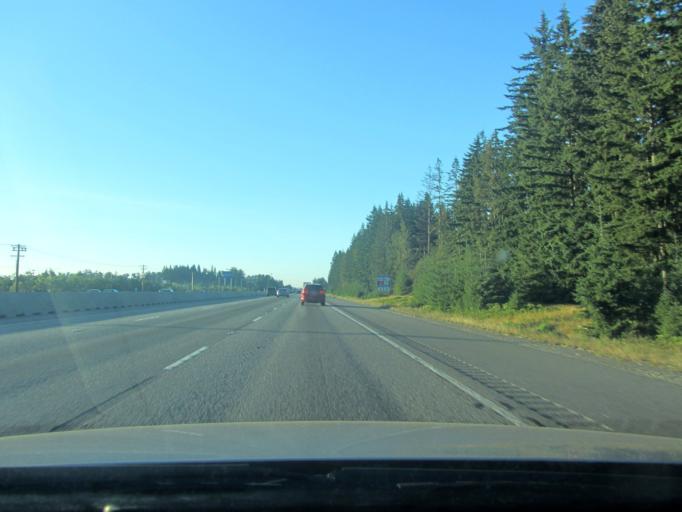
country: US
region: Washington
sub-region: Snohomish County
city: Marysville
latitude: 48.0880
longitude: -122.1847
